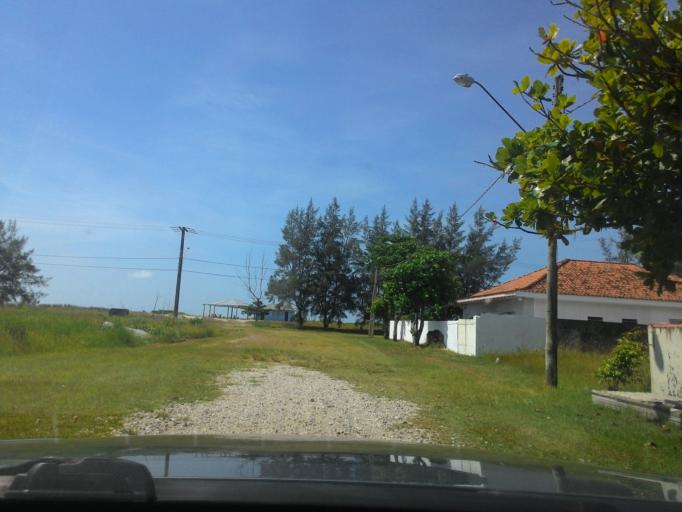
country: BR
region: Sao Paulo
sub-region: Iguape
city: Iguape
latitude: -24.8520
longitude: -47.6982
